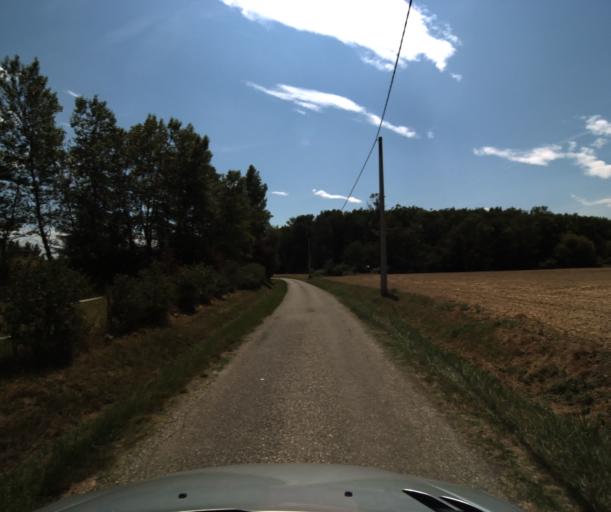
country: FR
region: Midi-Pyrenees
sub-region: Departement de la Haute-Garonne
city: Labastidette
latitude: 43.4644
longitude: 1.2342
